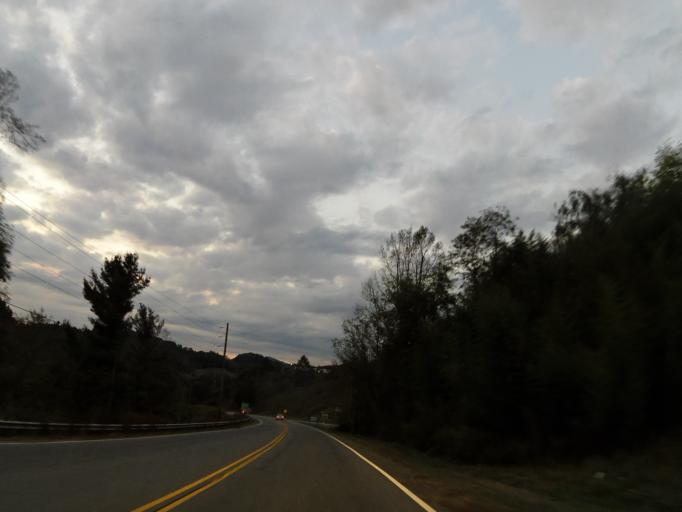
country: US
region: North Carolina
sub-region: Madison County
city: Marshall
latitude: 35.7996
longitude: -82.6556
